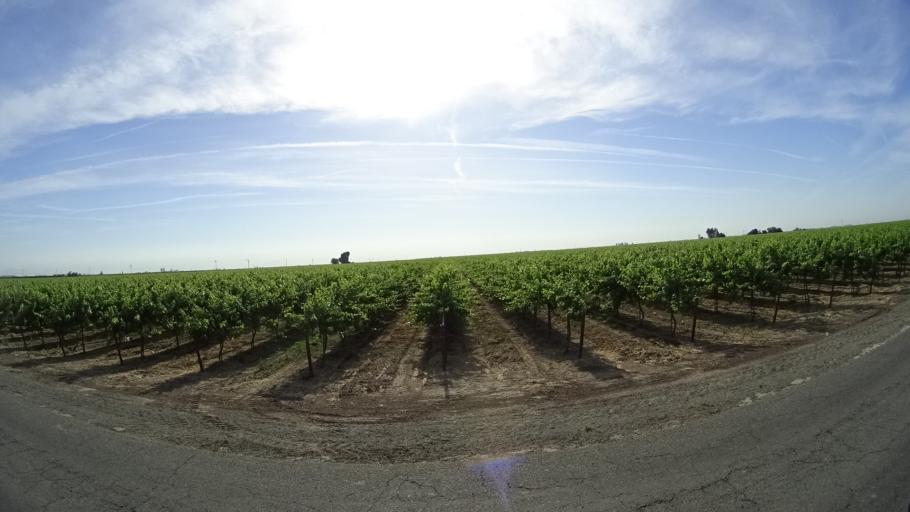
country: US
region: California
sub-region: Fresno County
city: Kingsburg
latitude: 36.4145
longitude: -119.5287
